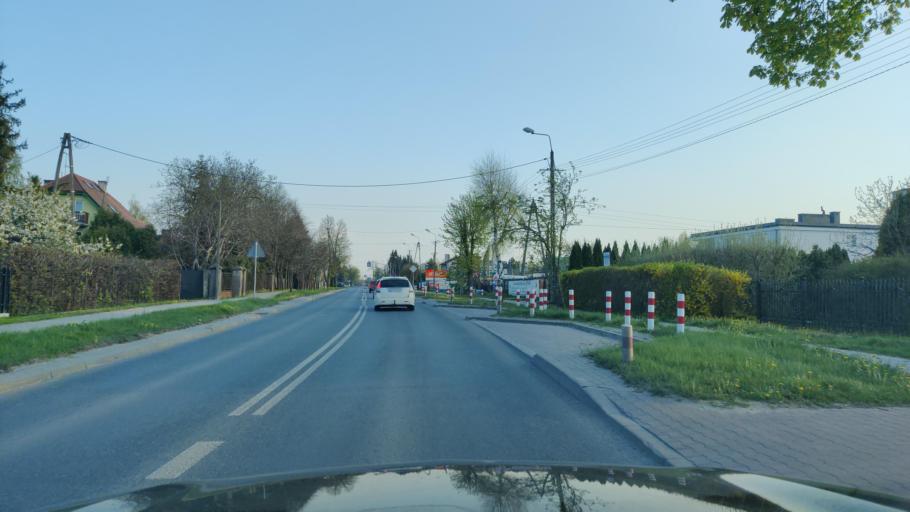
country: PL
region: Masovian Voivodeship
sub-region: Powiat pultuski
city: Pultusk
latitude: 52.6949
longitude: 21.0812
